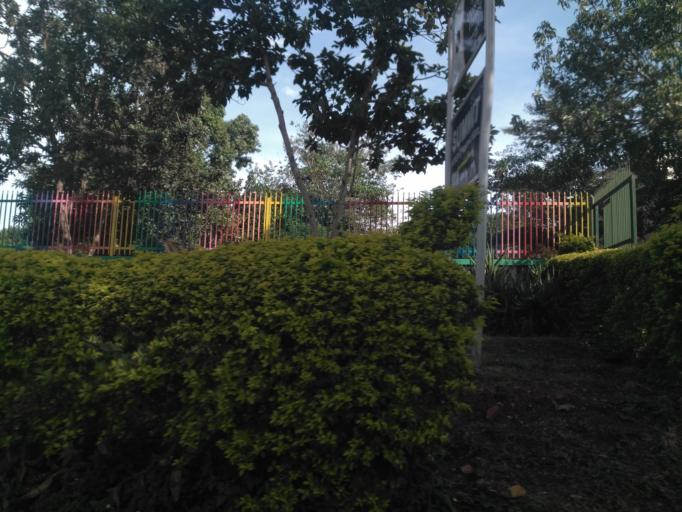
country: UG
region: Eastern Region
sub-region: Jinja District
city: Jinja
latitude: 0.4278
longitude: 33.2032
